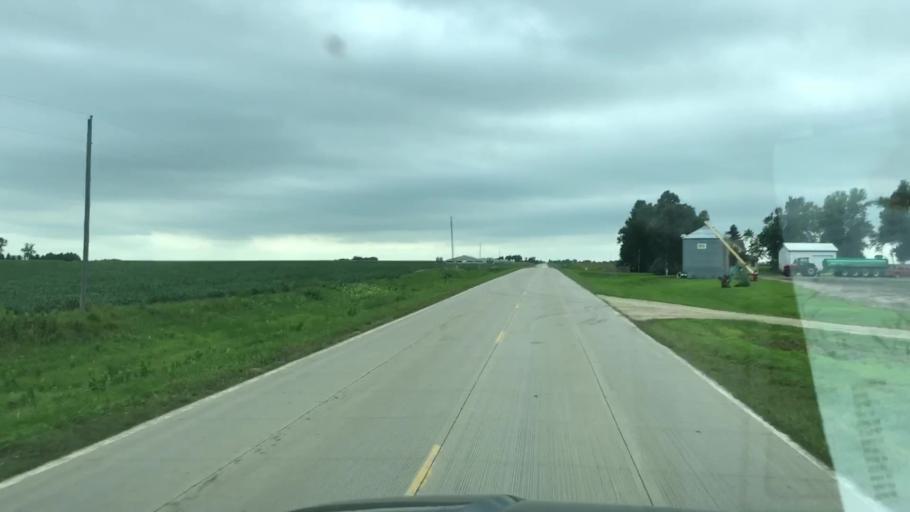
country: US
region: Iowa
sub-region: O'Brien County
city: Sheldon
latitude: 43.1336
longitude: -95.9792
